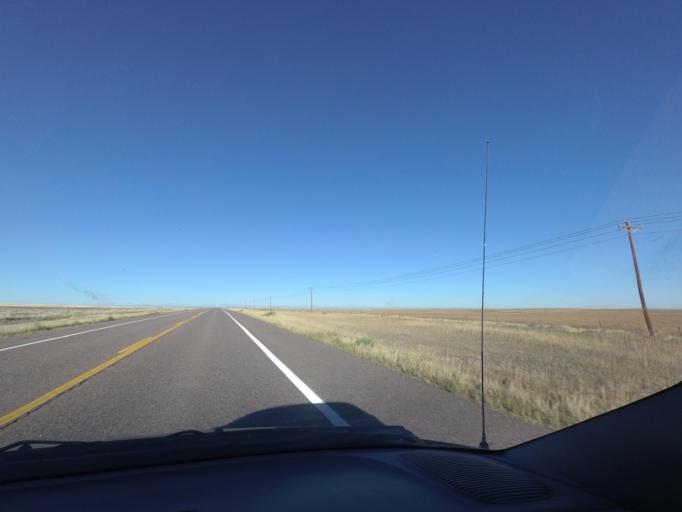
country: US
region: Colorado
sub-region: Arapahoe County
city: Byers
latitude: 39.7400
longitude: -104.0656
